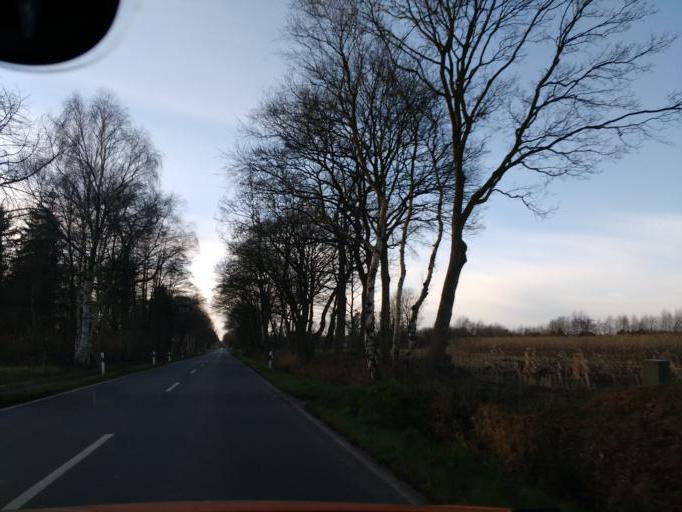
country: DE
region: Lower Saxony
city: Hude
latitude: 53.1065
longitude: 8.4339
